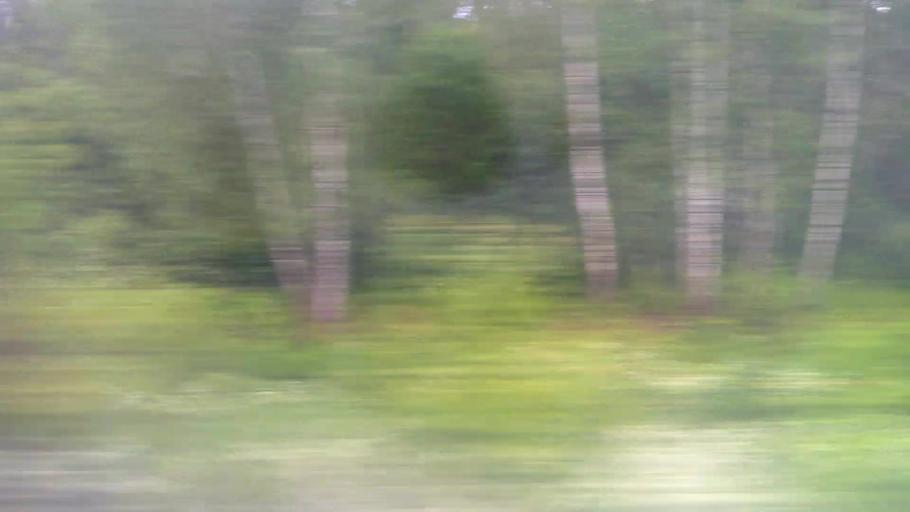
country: RU
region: Moskovskaya
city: Mikhnevo
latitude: 55.1840
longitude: 37.9306
